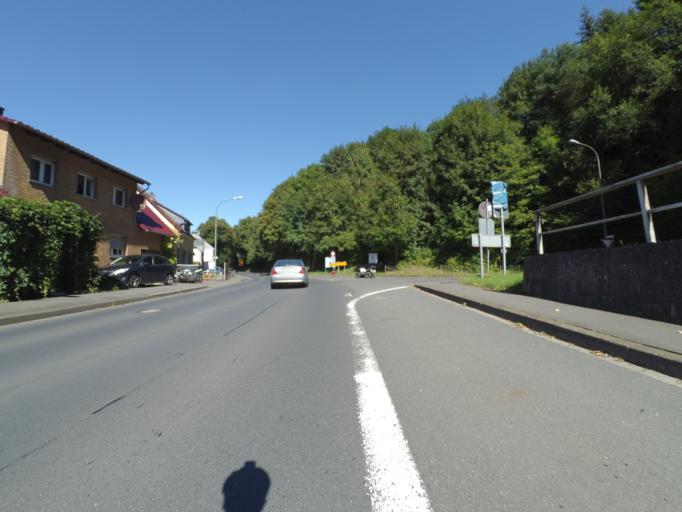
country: DE
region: Rheinland-Pfalz
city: Pelm
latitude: 50.2295
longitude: 6.6890
